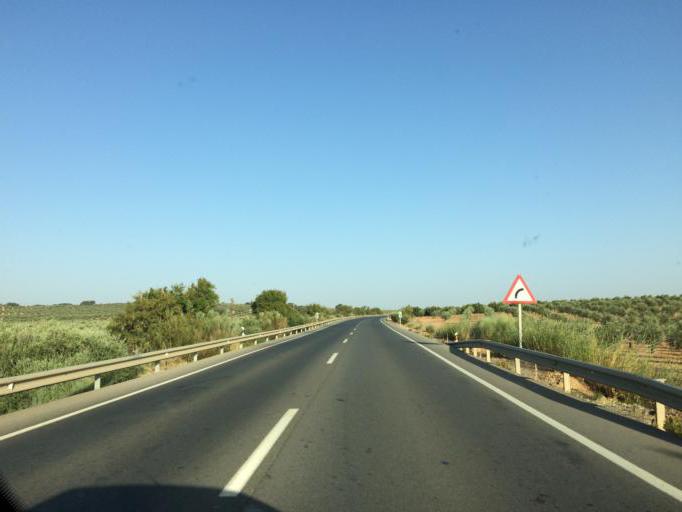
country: ES
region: Andalusia
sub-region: Provincia de Malaga
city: Humilladero
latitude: 37.0531
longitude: -4.6642
